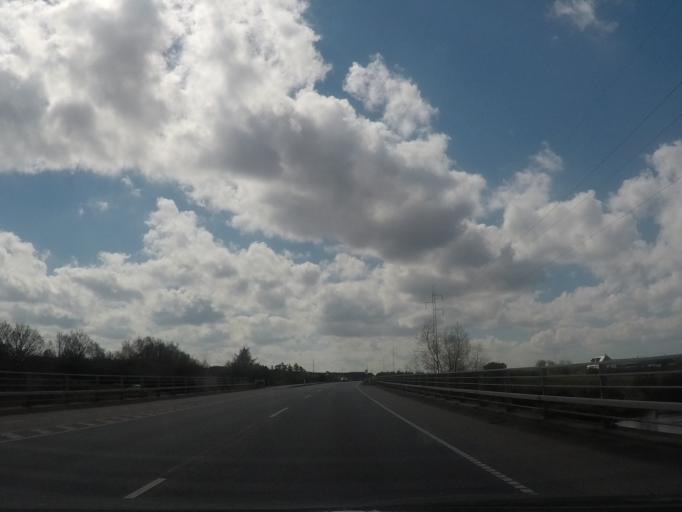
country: DK
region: South Denmark
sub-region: Kolding Kommune
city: Kolding
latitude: 55.5543
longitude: 9.4880
